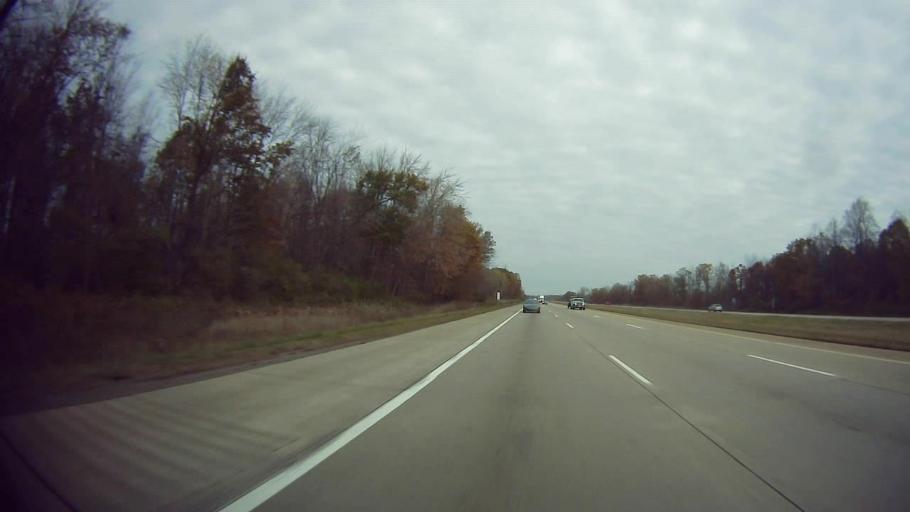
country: US
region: Michigan
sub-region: Monroe County
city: Carleton
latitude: 42.1011
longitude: -83.3779
